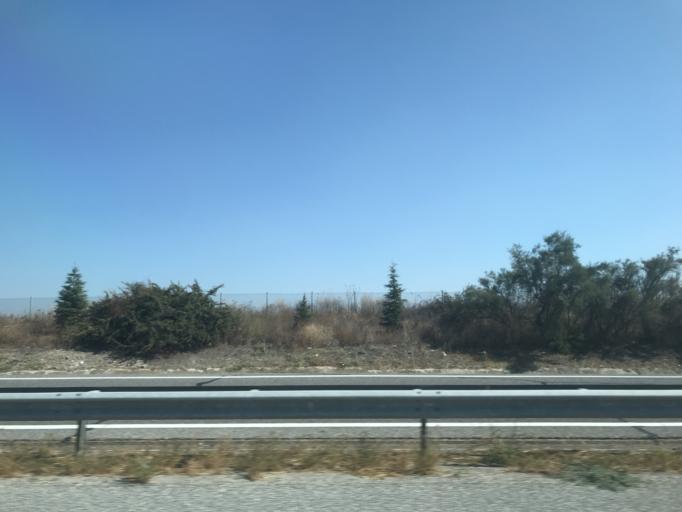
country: TR
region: Kirklareli
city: Luleburgaz
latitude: 41.3987
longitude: 27.3889
